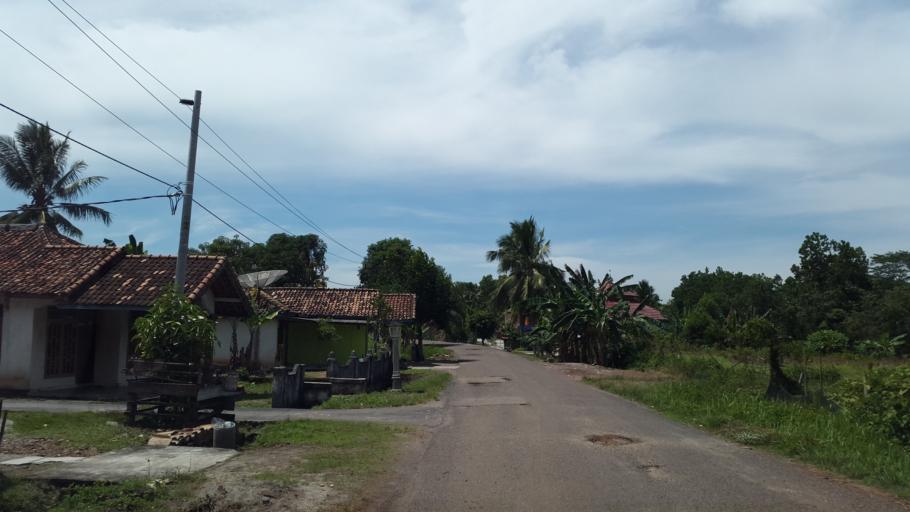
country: ID
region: South Sumatra
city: Kurungannyawa
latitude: -4.2257
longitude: 104.4659
